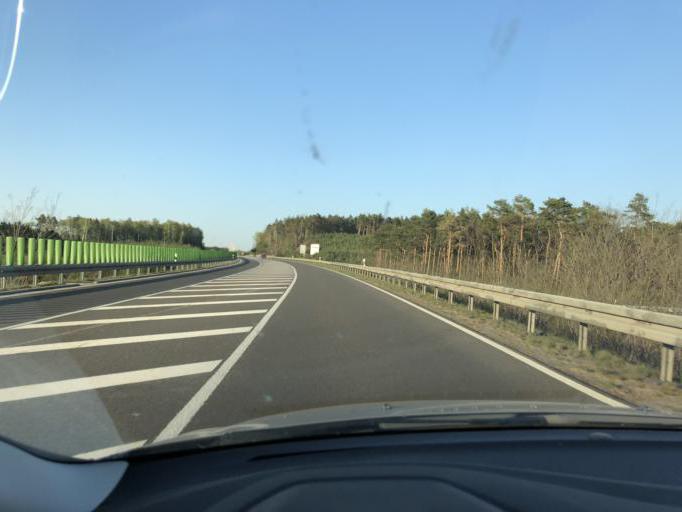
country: DE
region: Brandenburg
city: Schwarzbach
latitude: 51.4897
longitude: 13.9394
